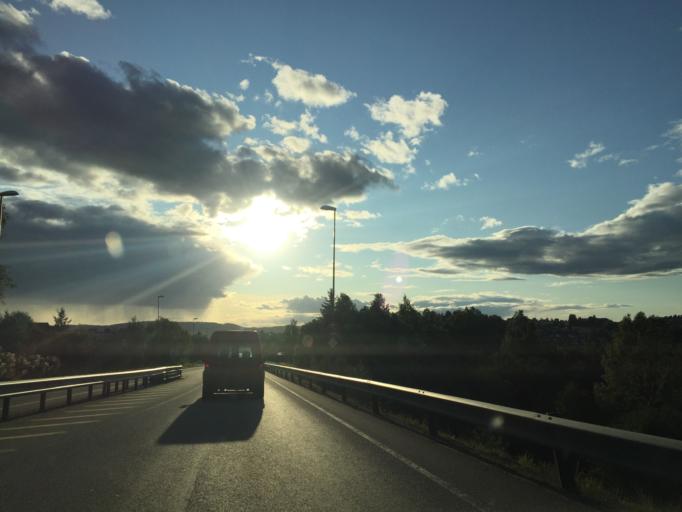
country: NO
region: Akershus
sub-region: Fet
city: Fetsund
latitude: 59.9225
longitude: 11.1805
